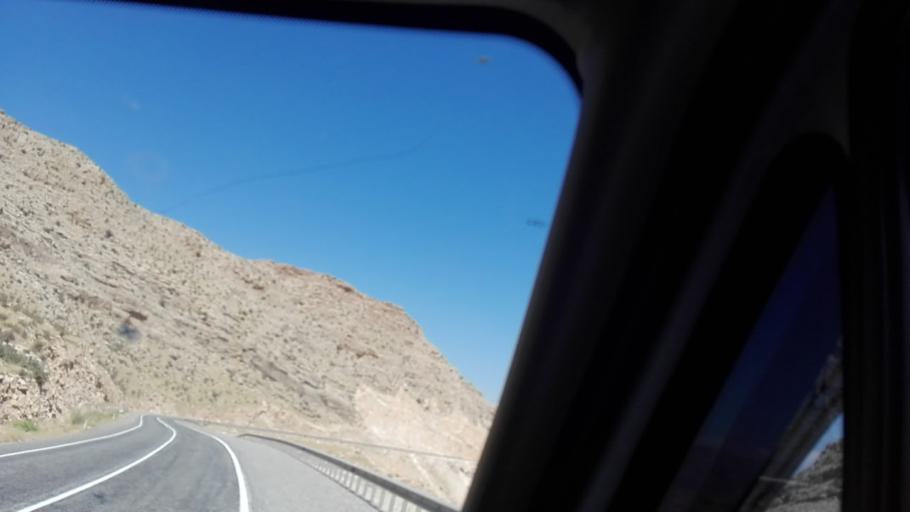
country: TR
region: Batman
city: Hasankeyf
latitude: 37.6954
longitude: 41.4589
